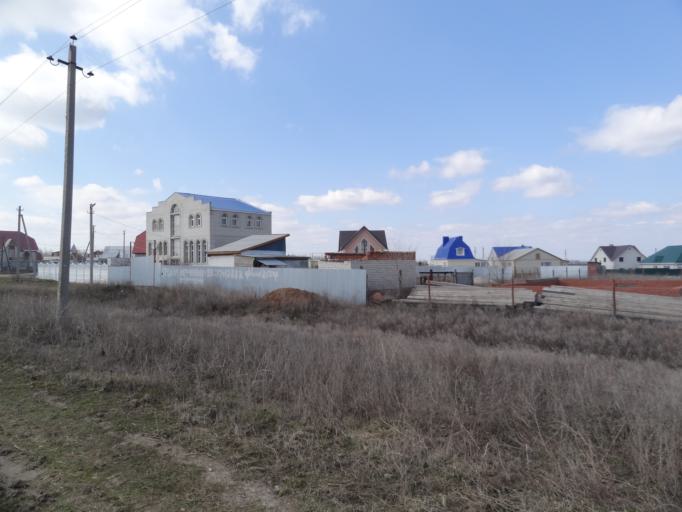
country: RU
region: Saratov
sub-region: Saratovskiy Rayon
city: Saratov
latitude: 51.6671
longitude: 46.0645
